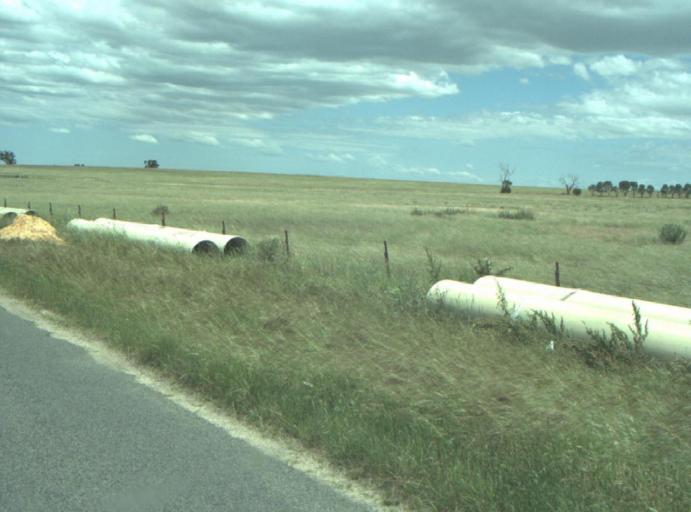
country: AU
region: Victoria
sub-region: Wyndham
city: Little River
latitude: -37.9358
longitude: 144.4657
